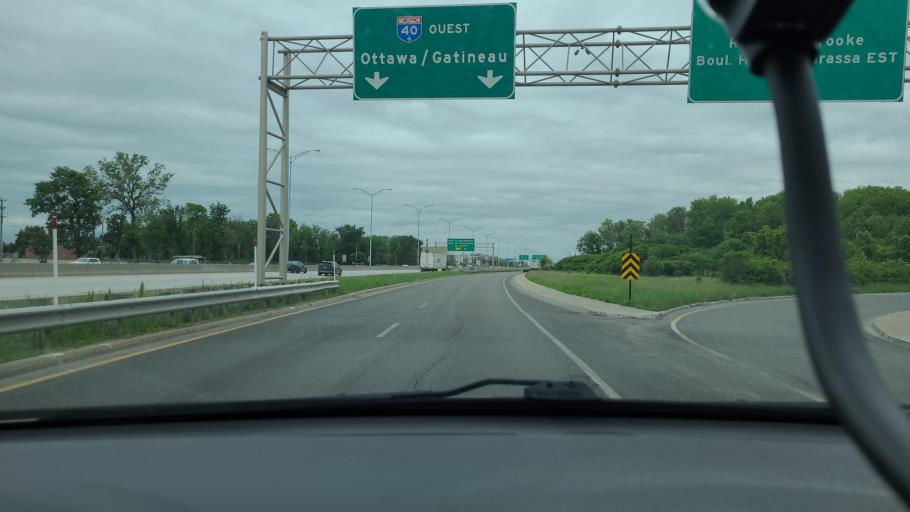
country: CA
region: Quebec
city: Montreal-Est
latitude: 45.6588
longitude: -73.5195
